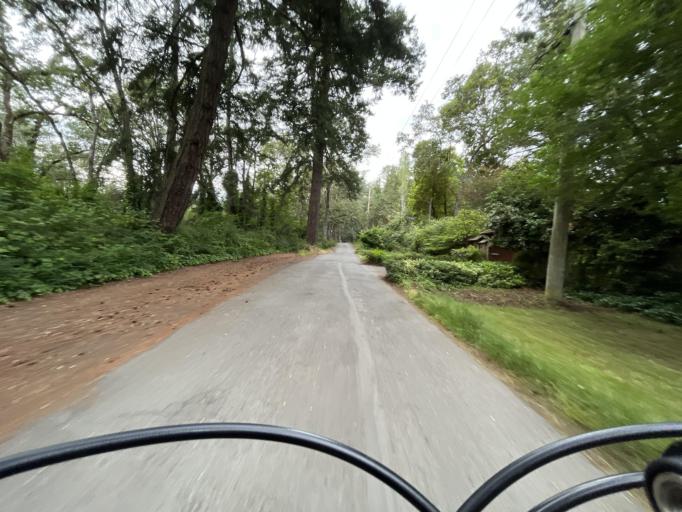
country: CA
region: British Columbia
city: Oak Bay
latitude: 48.4813
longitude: -123.3459
